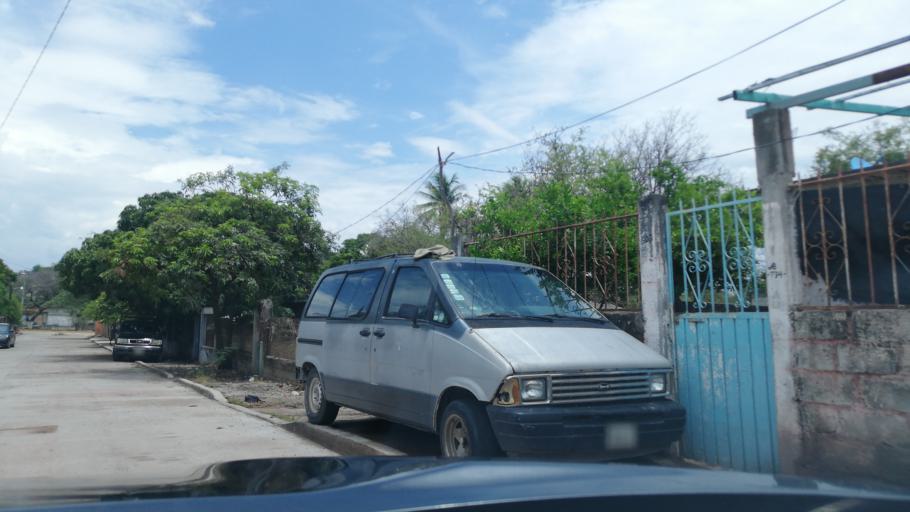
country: MX
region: Oaxaca
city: Santa Maria Jalapa del Marques
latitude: 16.4439
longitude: -95.4416
